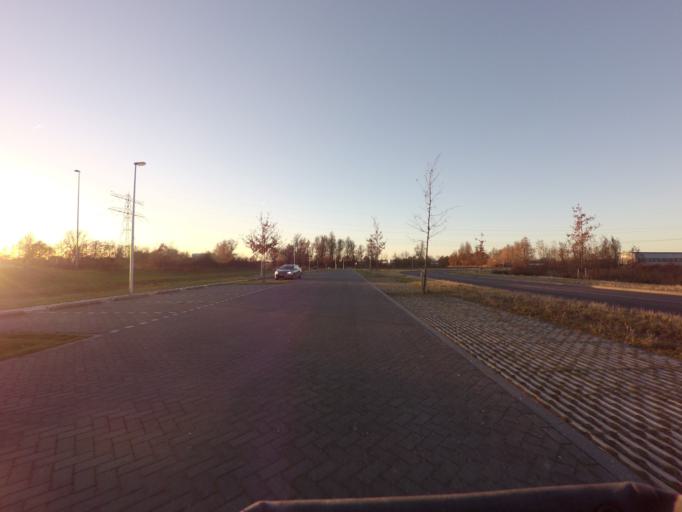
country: NL
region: Utrecht
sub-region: Gemeente Nieuwegein
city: Nieuwegein
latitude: 52.0765
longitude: 5.0632
